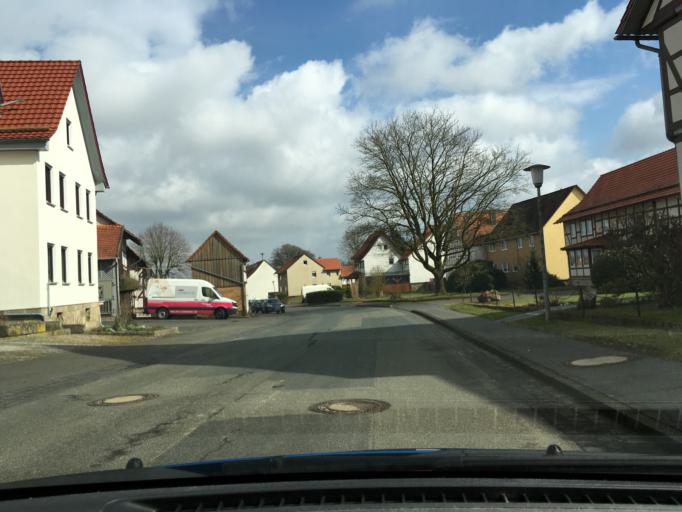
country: DE
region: Lower Saxony
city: Buhren
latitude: 51.5106
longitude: 9.6778
